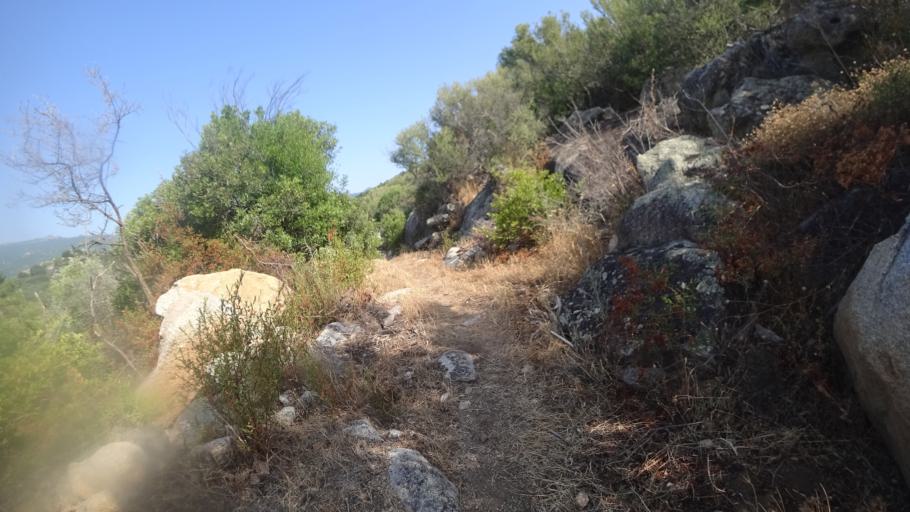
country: FR
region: Corsica
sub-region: Departement de la Corse-du-Sud
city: Porto-Vecchio
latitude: 41.6647
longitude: 9.3264
